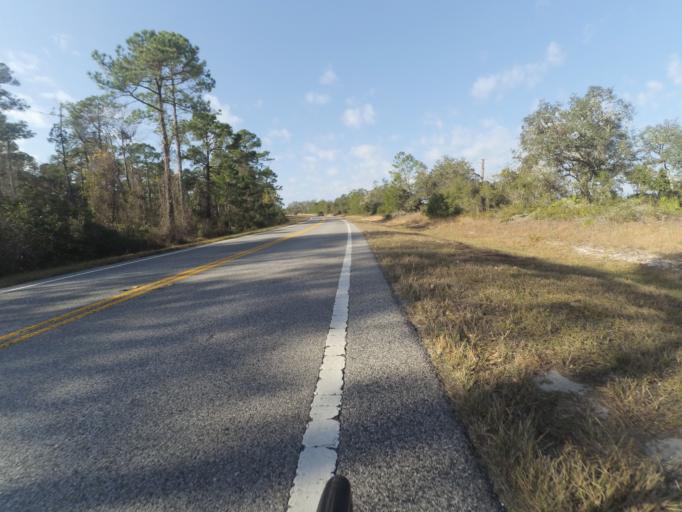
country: US
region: Florida
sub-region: Lake County
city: Astor
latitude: 29.1425
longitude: -81.5938
